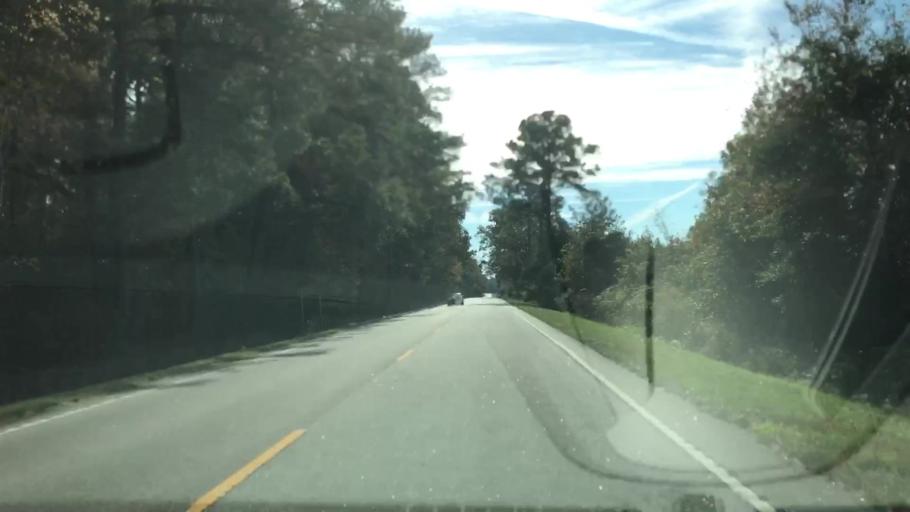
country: US
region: South Carolina
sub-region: Colleton County
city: Walterboro
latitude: 32.8459
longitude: -80.5916
